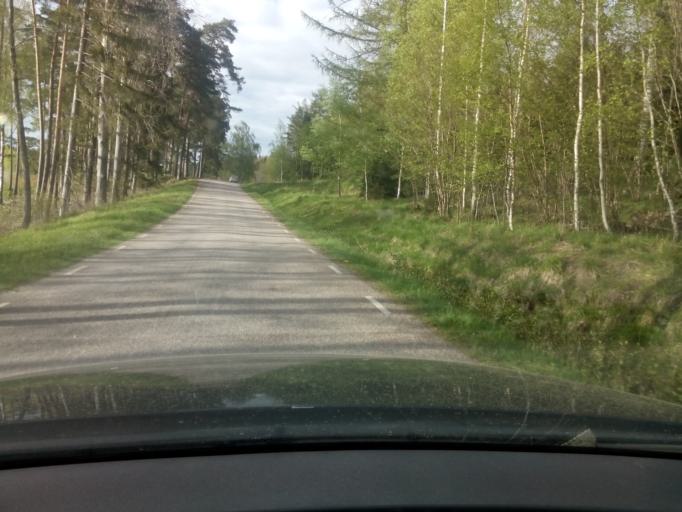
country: SE
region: Soedermanland
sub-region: Nykopings Kommun
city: Stigtomta
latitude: 58.9349
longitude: 16.8902
